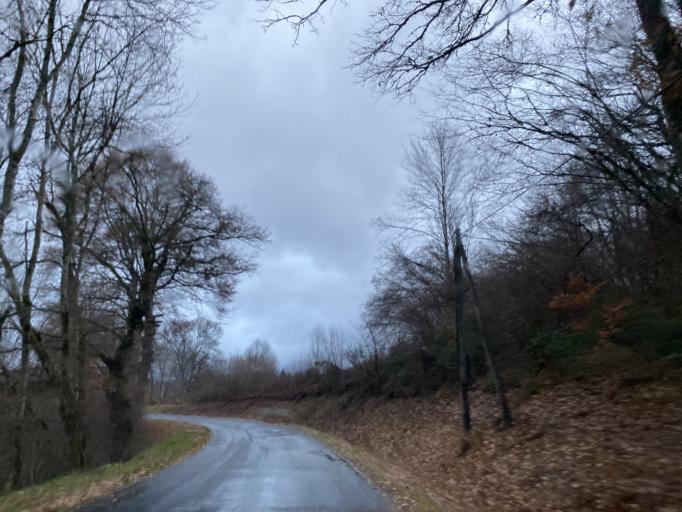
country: FR
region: Auvergne
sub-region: Departement du Puy-de-Dome
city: La Monnerie-le-Montel
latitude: 45.8539
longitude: 3.6137
